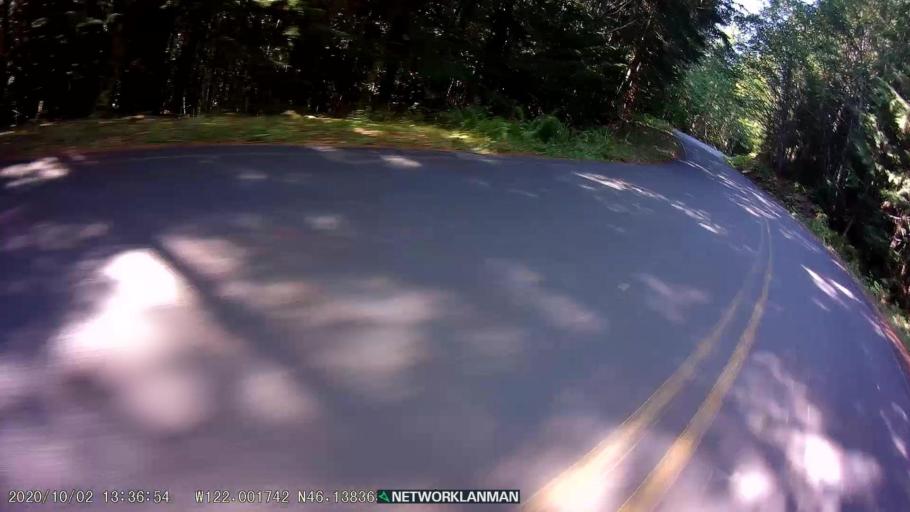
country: US
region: Washington
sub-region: Skamania County
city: Carson
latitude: 46.1385
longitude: -122.0018
